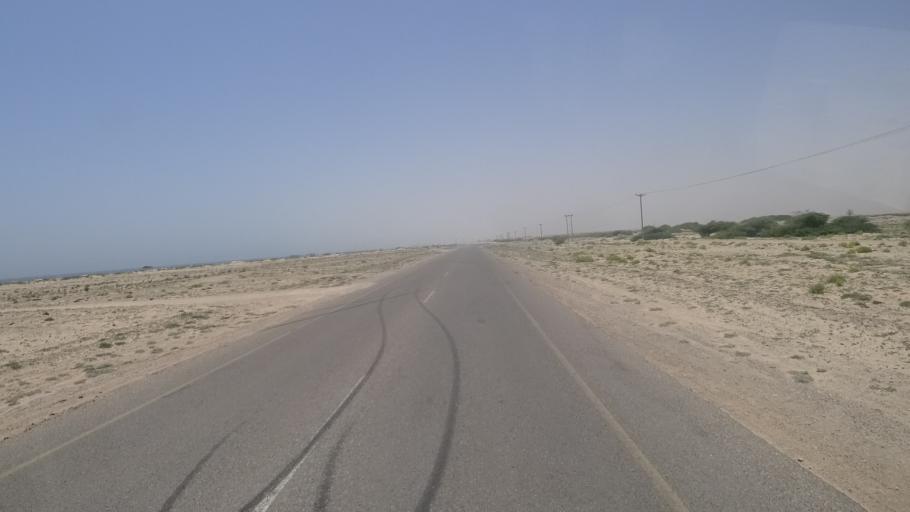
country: OM
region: Ash Sharqiyah
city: Sur
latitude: 22.1017
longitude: 59.7034
